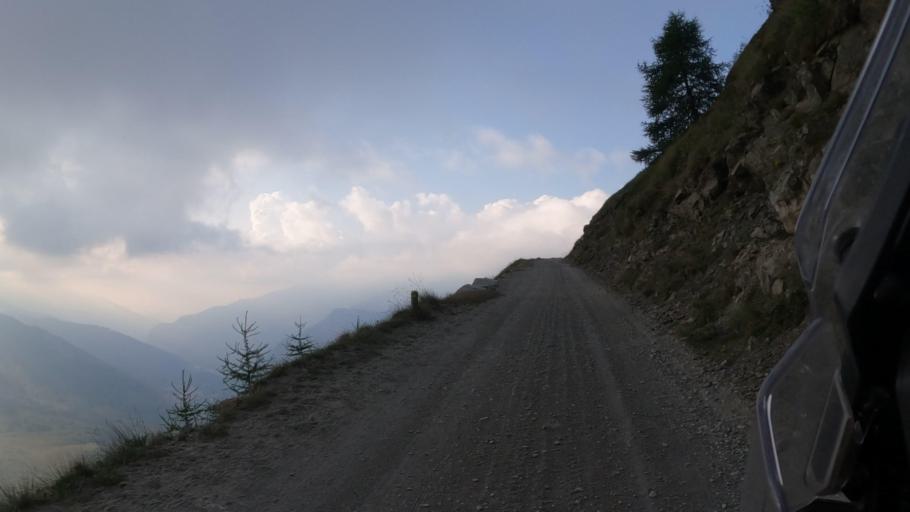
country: IT
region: Piedmont
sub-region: Provincia di Torino
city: Usseaux
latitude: 45.0601
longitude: 7.0034
